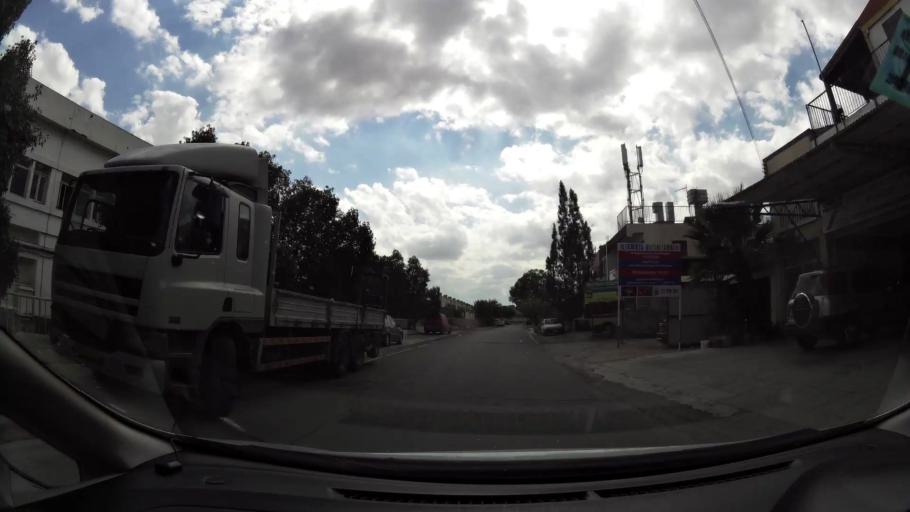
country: CY
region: Lefkosia
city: Nicosia
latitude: 35.1807
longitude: 33.3912
